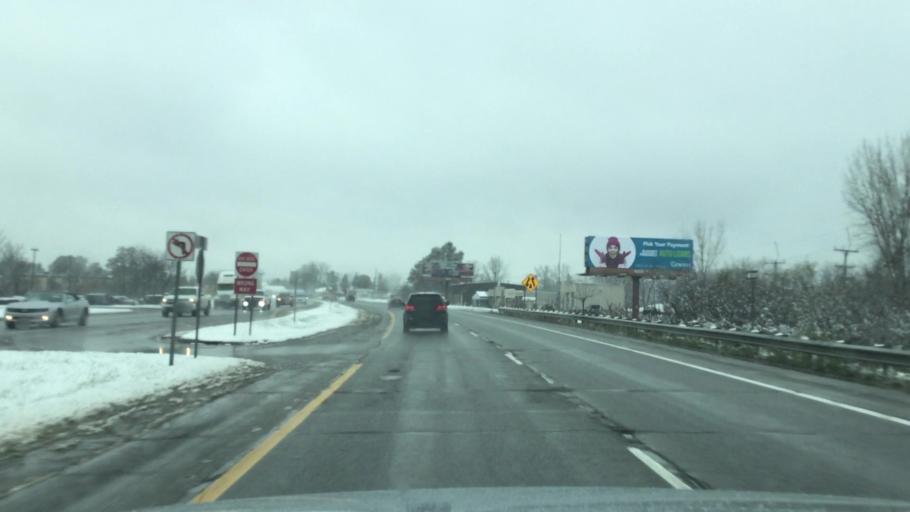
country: US
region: Michigan
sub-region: Oakland County
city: Lake Orion
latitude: 42.8046
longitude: -83.2479
